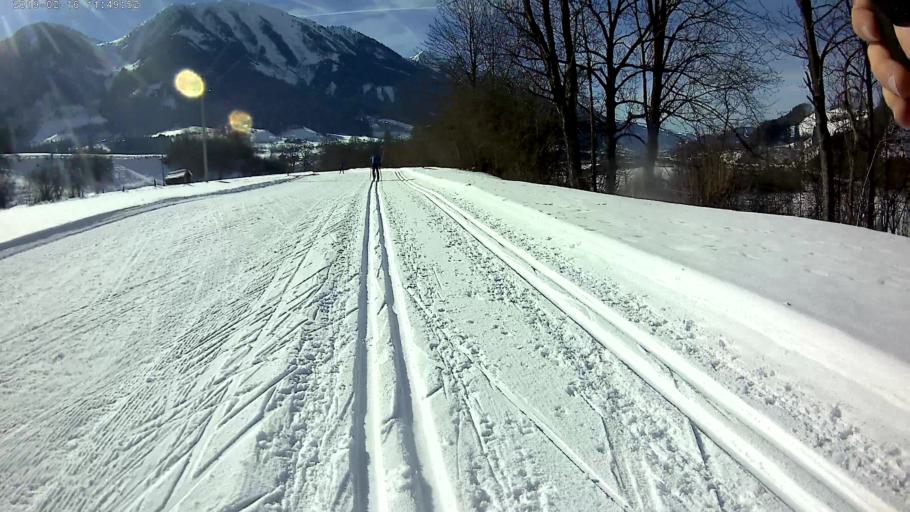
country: AT
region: Salzburg
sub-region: Politischer Bezirk Sankt Johann im Pongau
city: Sankt Johann im Pongau
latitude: 47.3291
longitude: 13.1899
